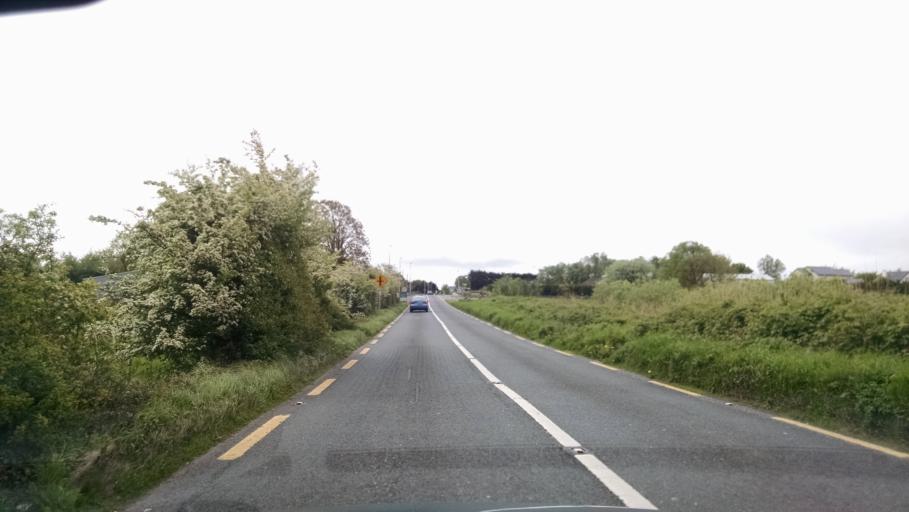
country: IE
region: Connaught
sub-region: County Galway
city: Claregalway
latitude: 53.3802
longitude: -9.0161
